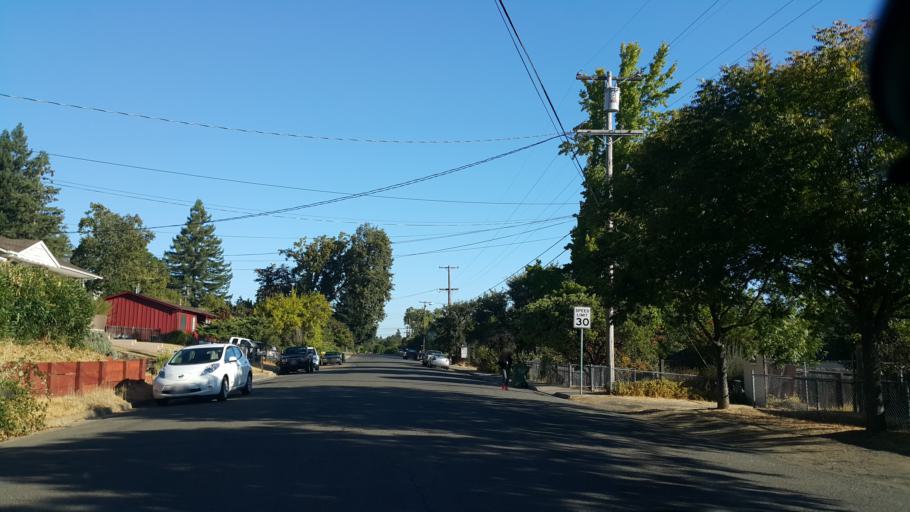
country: US
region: California
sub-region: Mendocino County
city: Ukiah
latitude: 39.1368
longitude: -123.2145
